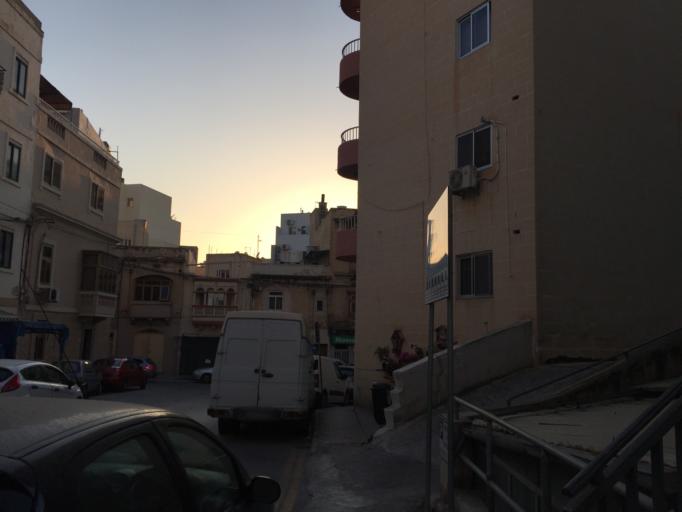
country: MT
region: Tal-Pieta
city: Pieta
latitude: 35.8941
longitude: 14.4915
